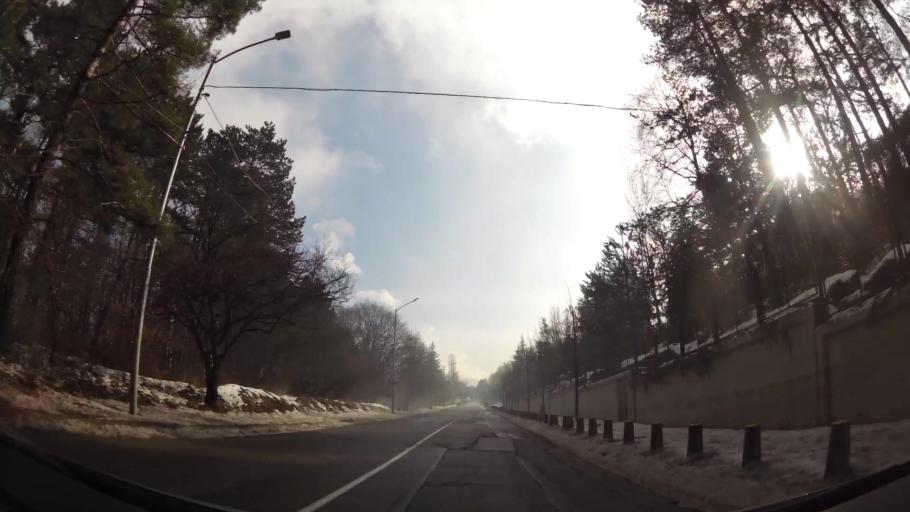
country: BG
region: Sofia-Capital
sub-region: Stolichna Obshtina
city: Sofia
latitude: 42.6484
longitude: 23.2438
